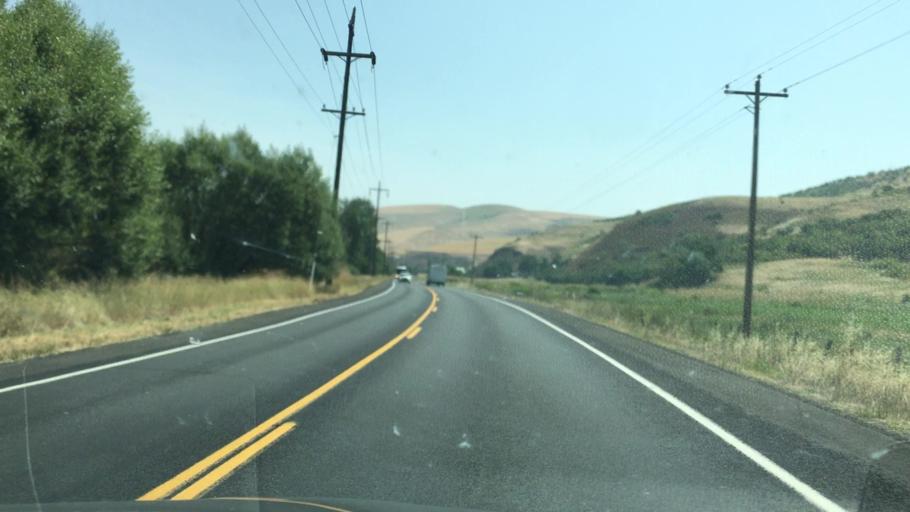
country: US
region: Idaho
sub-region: Nez Perce County
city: Lapwai
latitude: 46.3581
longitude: -116.7875
